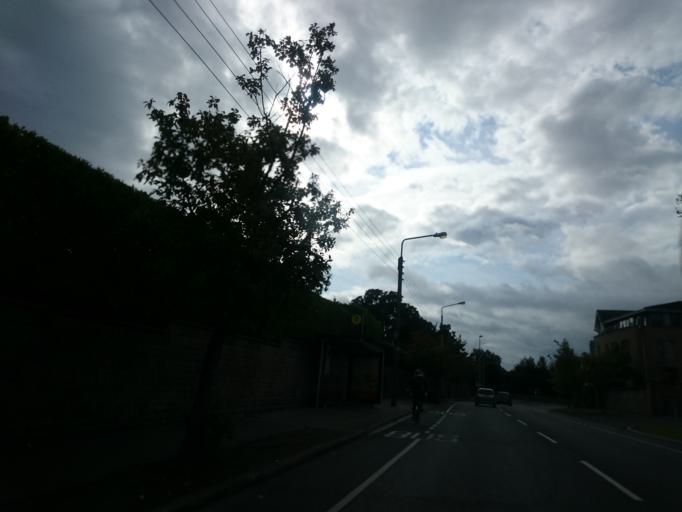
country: IE
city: Clonskeagh
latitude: 53.3037
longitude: -6.2344
